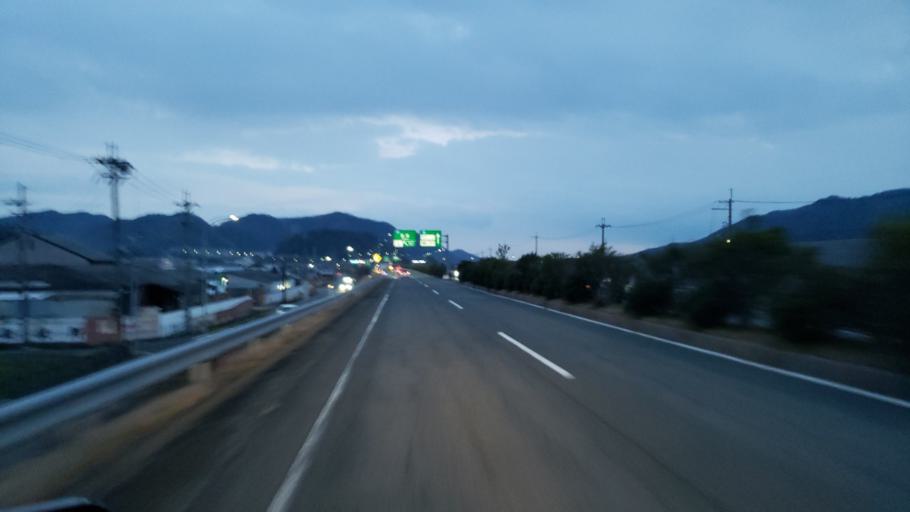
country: JP
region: Hyogo
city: Himeji
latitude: 34.8815
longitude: 134.7414
